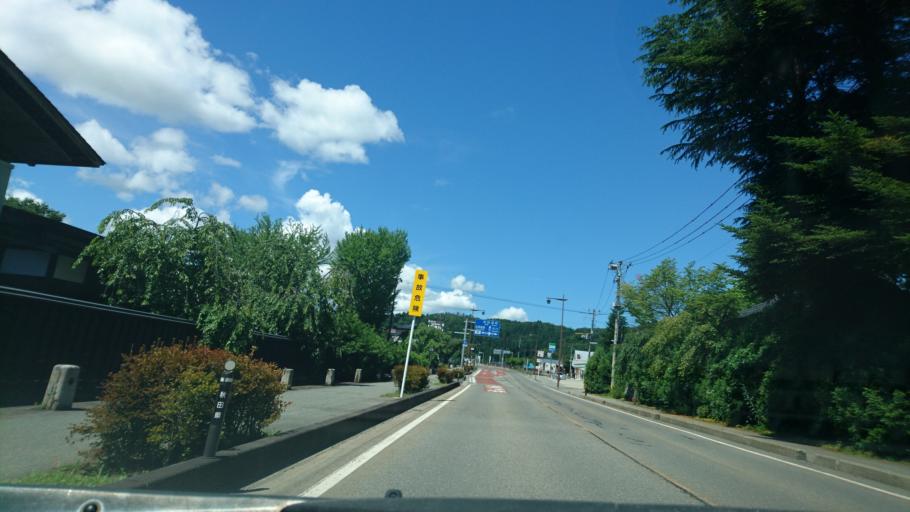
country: JP
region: Akita
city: Kakunodatemachi
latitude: 39.6028
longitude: 140.5611
